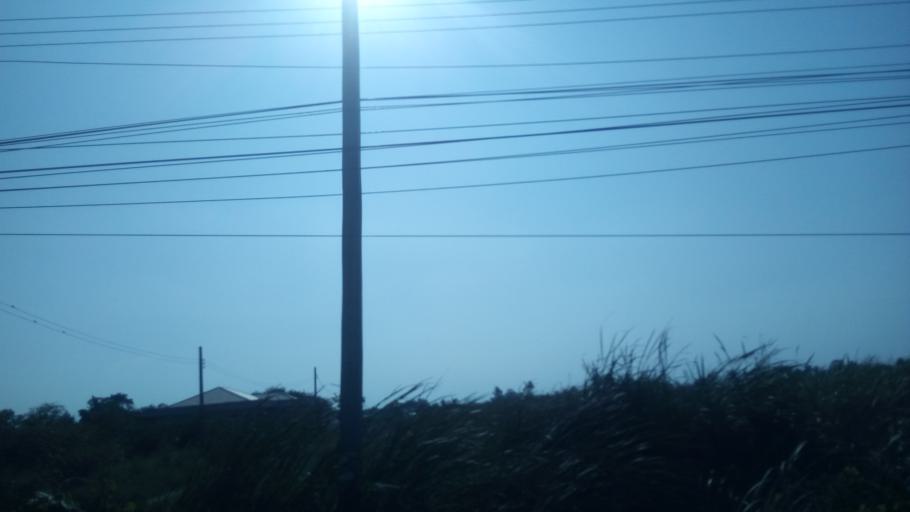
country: TH
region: Nonthaburi
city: Bang Yai
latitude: 13.8935
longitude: 100.3256
